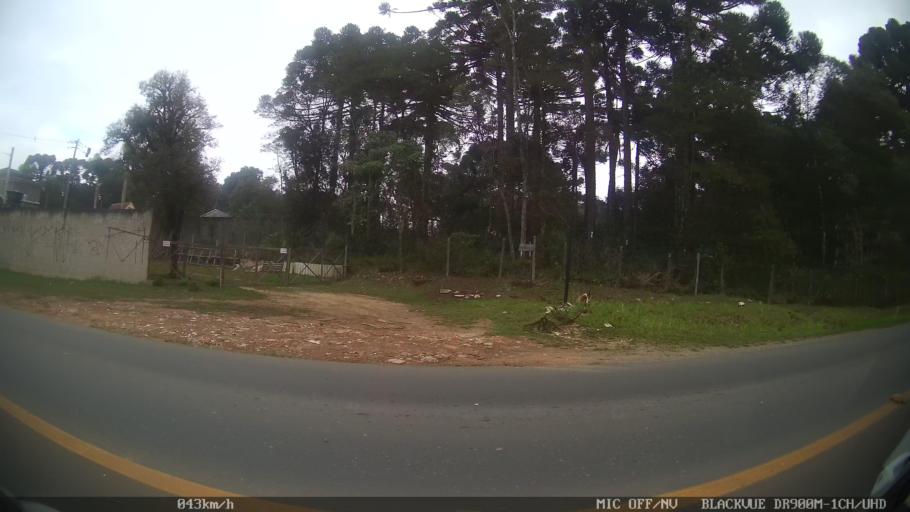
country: BR
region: Parana
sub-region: Curitiba
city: Curitiba
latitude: -25.3879
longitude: -49.3216
